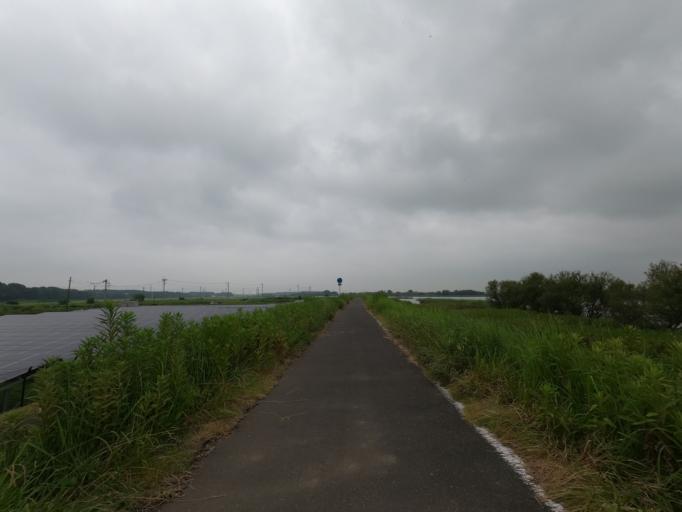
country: JP
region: Ibaraki
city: Moriya
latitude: 35.9319
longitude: 140.0425
